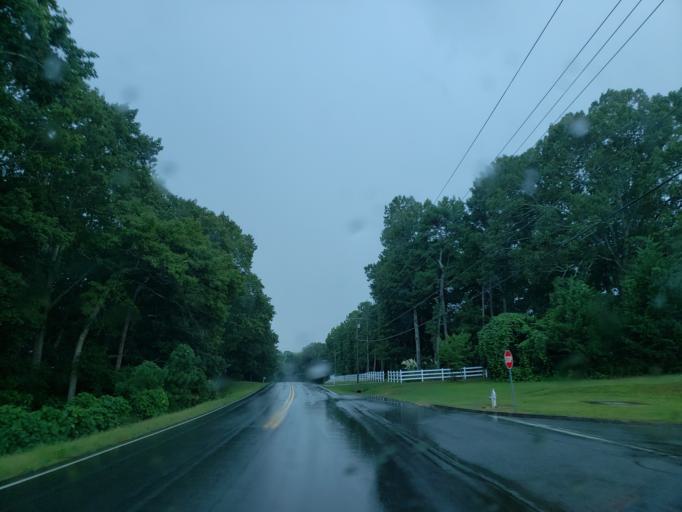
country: US
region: Georgia
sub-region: Cherokee County
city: Canton
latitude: 34.3242
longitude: -84.4688
